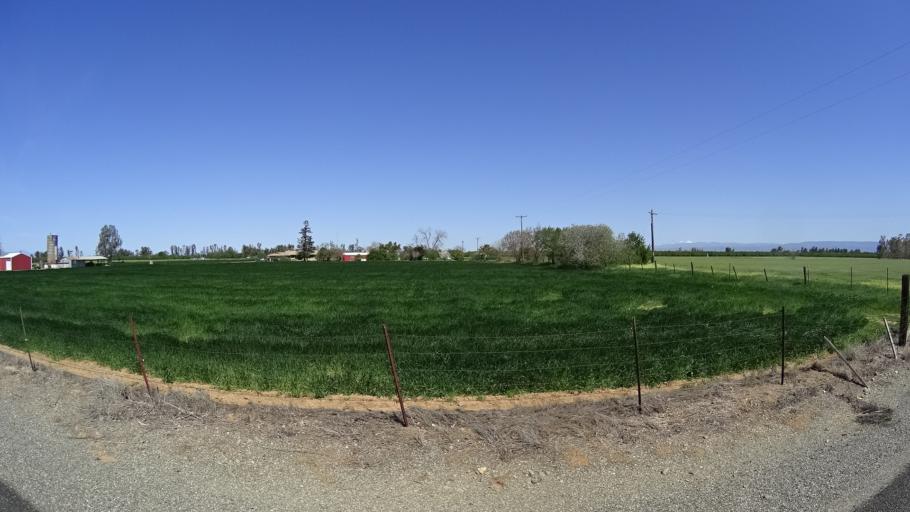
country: US
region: California
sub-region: Glenn County
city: Hamilton City
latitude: 39.7896
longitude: -122.0901
